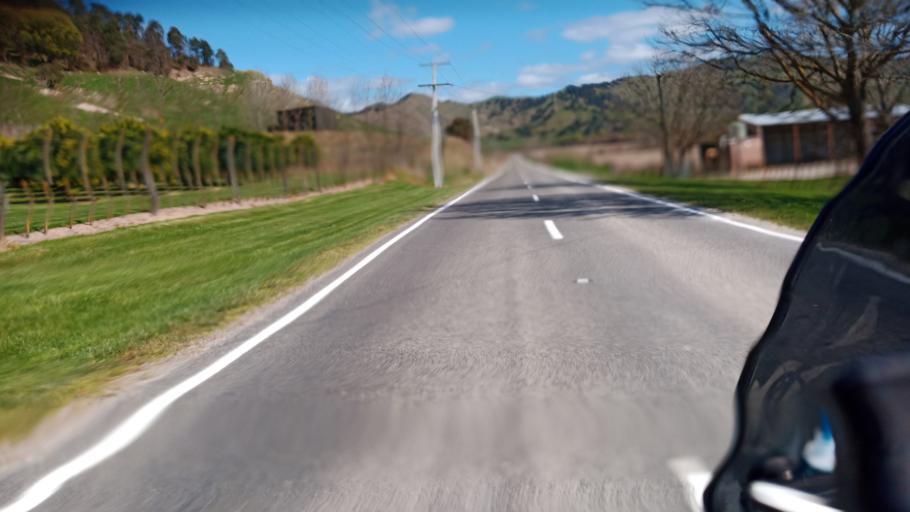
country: NZ
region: Gisborne
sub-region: Gisborne District
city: Gisborne
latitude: -38.7060
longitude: 177.8400
